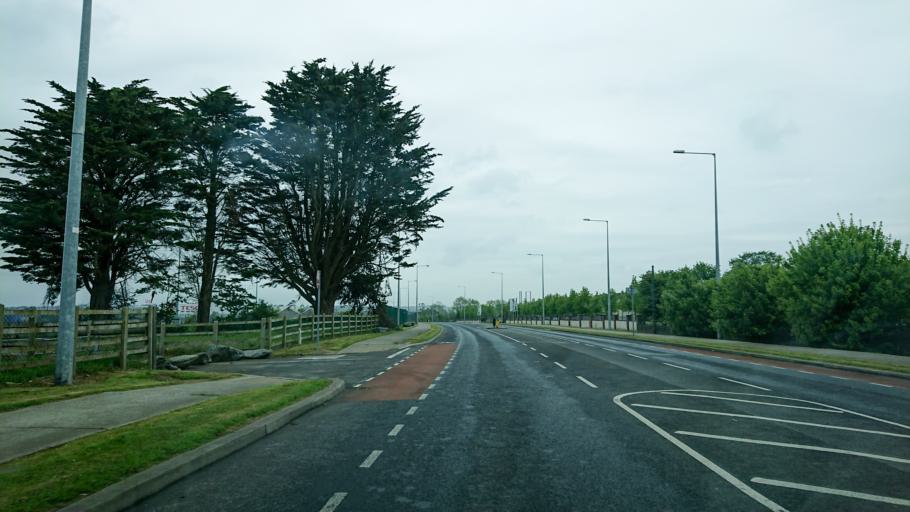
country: IE
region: Munster
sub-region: Waterford
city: Waterford
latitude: 52.2341
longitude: -7.1406
